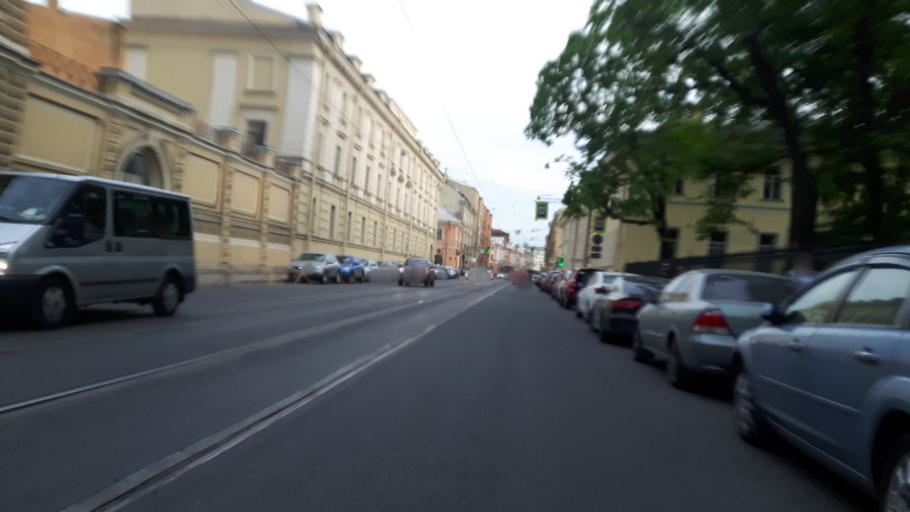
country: RU
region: St.-Petersburg
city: Saint Petersburg
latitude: 59.9387
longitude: 30.3366
